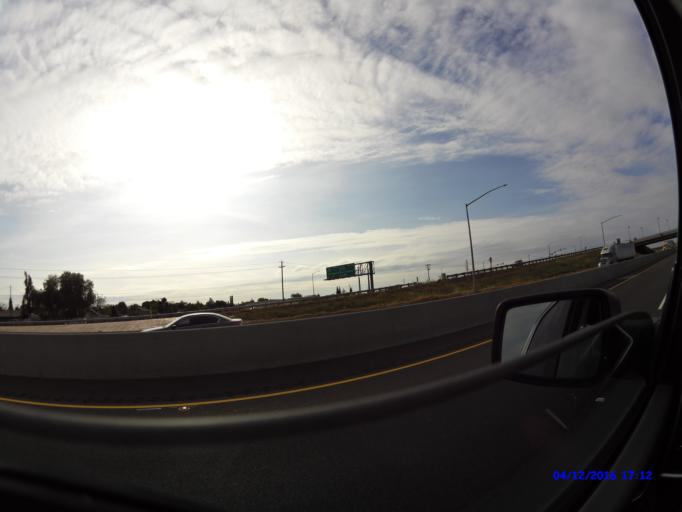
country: US
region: California
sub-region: San Joaquin County
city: Manteca
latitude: 37.8248
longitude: -121.2169
